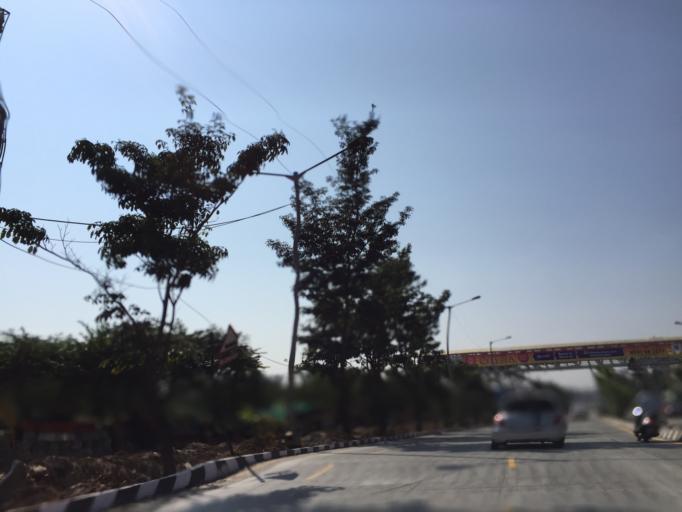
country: IN
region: Karnataka
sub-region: Bangalore Urban
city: Bangalore
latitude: 13.0051
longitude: 77.6631
